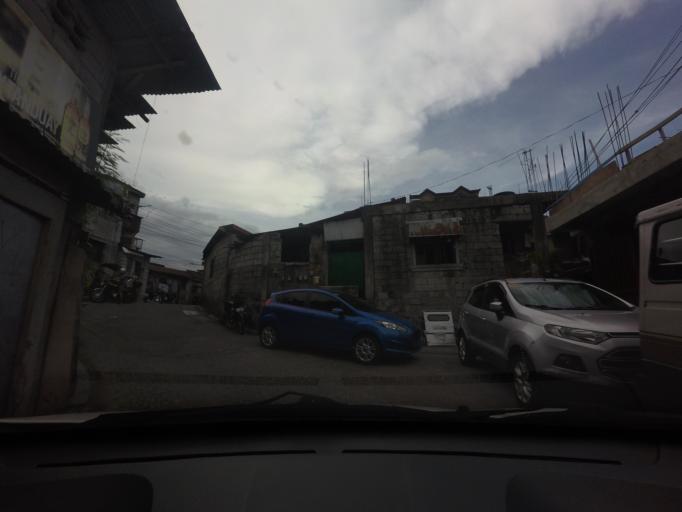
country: PH
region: Calabarzon
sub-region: Province of Rizal
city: Pateros
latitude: 14.5530
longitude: 121.0613
